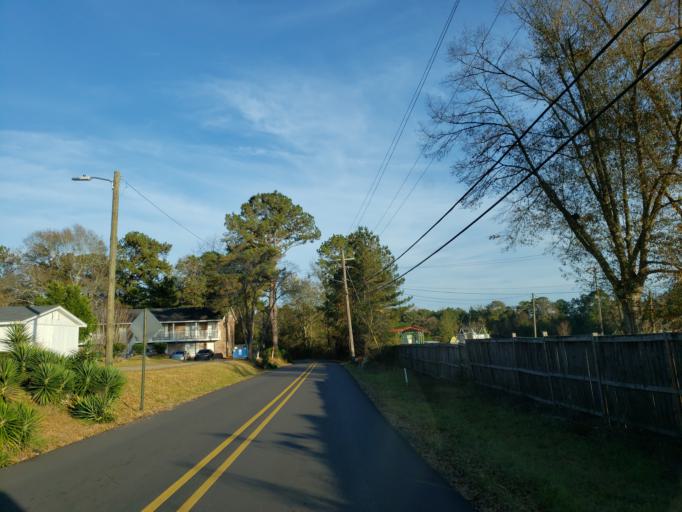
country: US
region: Mississippi
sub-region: Lamar County
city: Arnold Line
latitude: 31.3481
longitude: -89.3604
